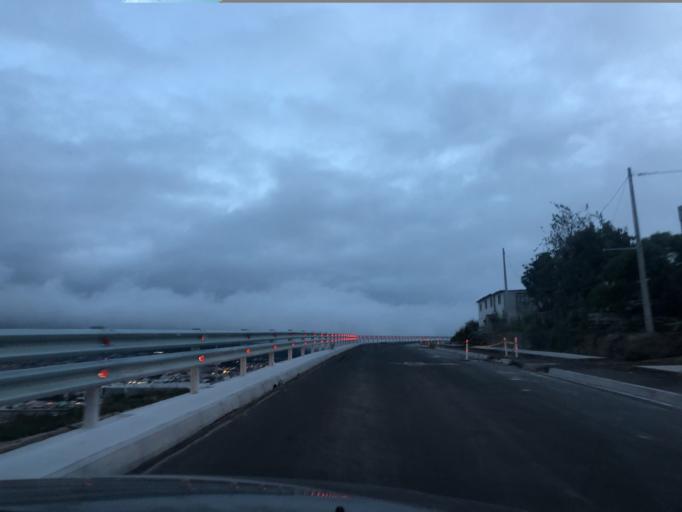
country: EC
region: Imbabura
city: Ibarra
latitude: 0.3724
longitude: -78.1285
